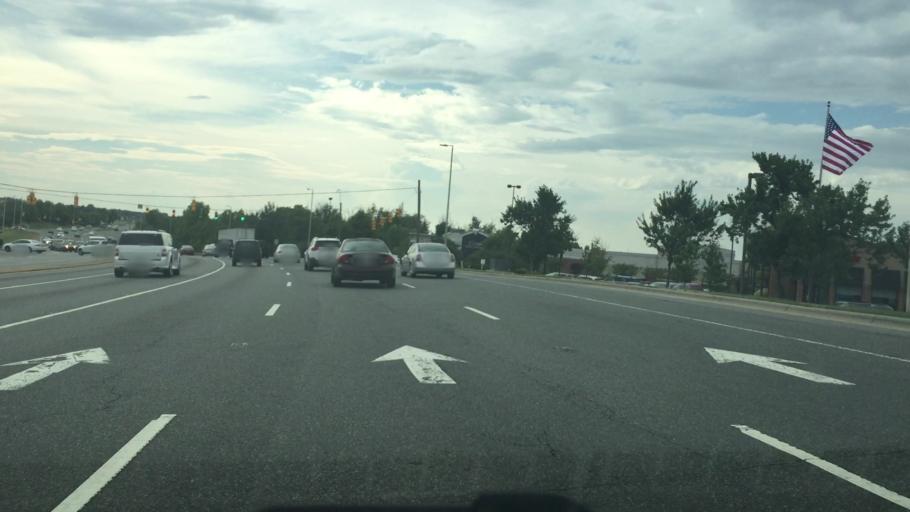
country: US
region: North Carolina
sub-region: Cabarrus County
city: Harrisburg
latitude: 35.3710
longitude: -80.7174
